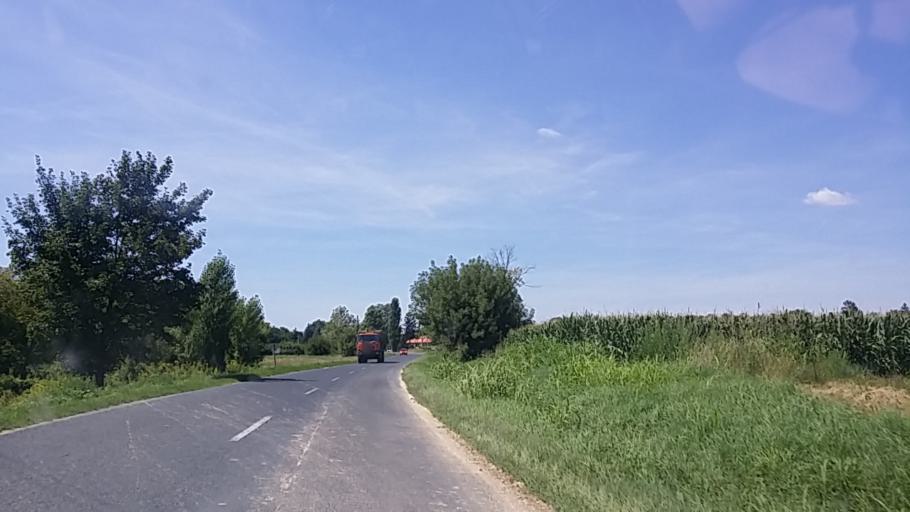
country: HU
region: Somogy
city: Tab
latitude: 46.7148
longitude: 17.9838
